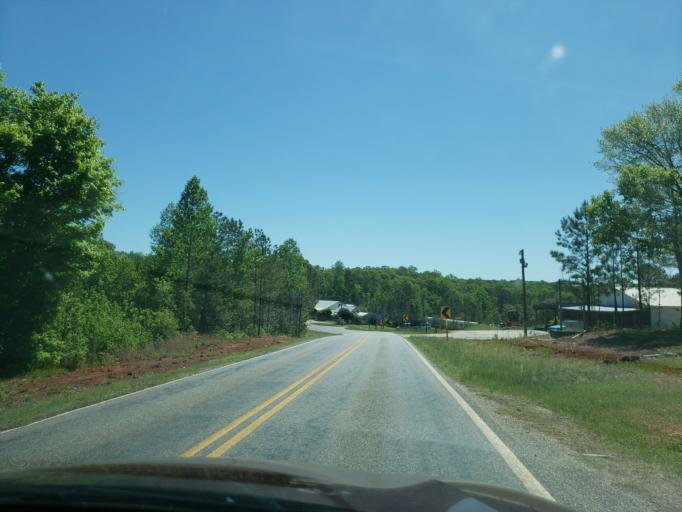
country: US
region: Alabama
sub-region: Tallapoosa County
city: Dadeville
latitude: 32.7057
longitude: -85.8118
